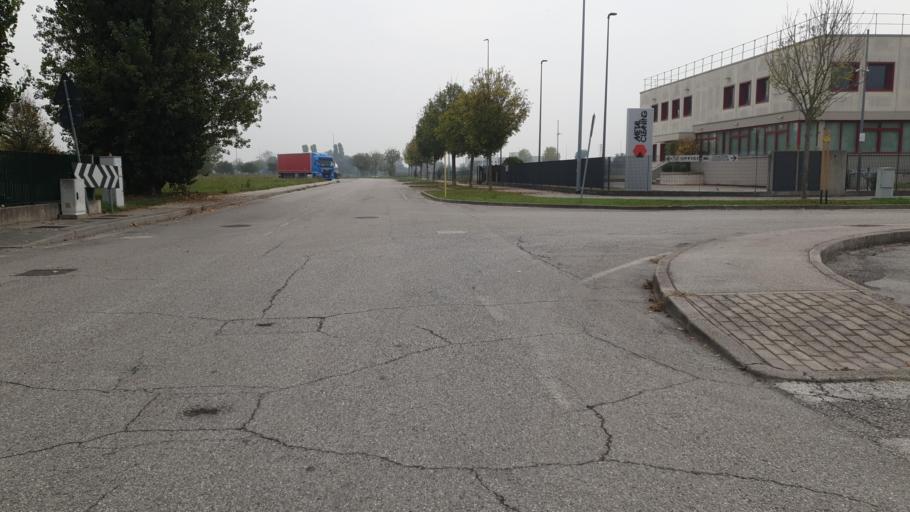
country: IT
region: Veneto
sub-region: Provincia di Padova
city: Casalserugo
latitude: 45.3090
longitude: 11.9128
